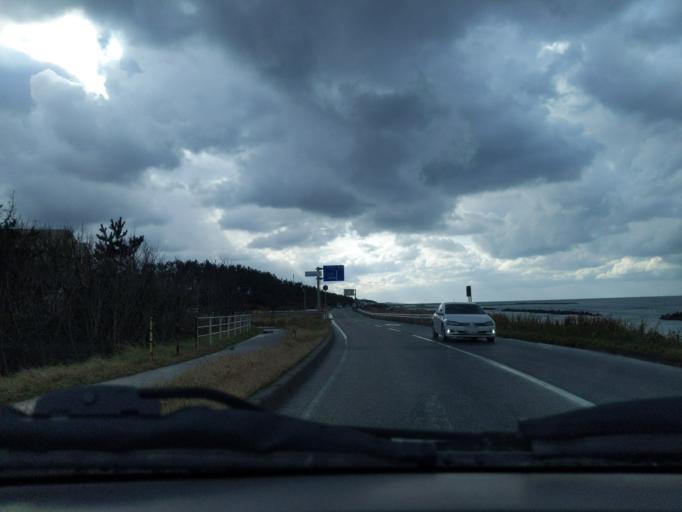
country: JP
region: Niigata
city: Niigata-shi
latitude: 37.9267
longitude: 139.0311
